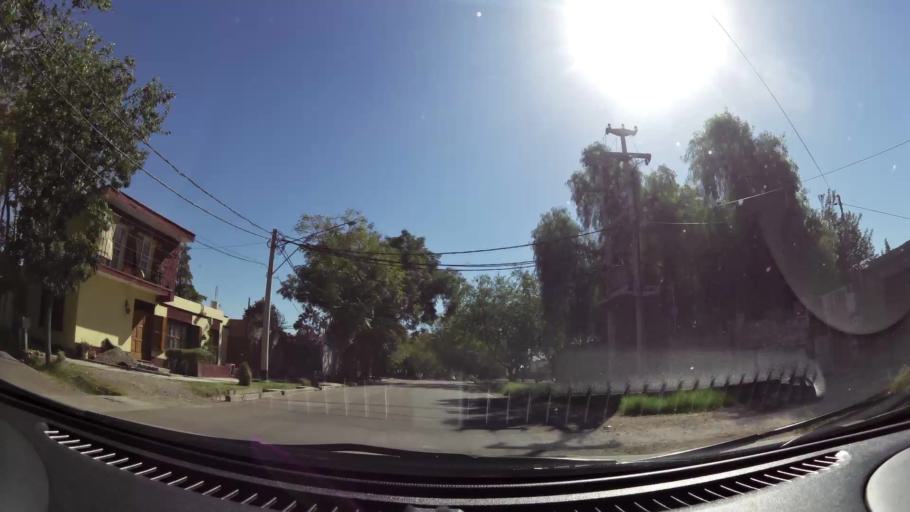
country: AR
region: Mendoza
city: Mendoza
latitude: -32.8817
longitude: -68.8069
